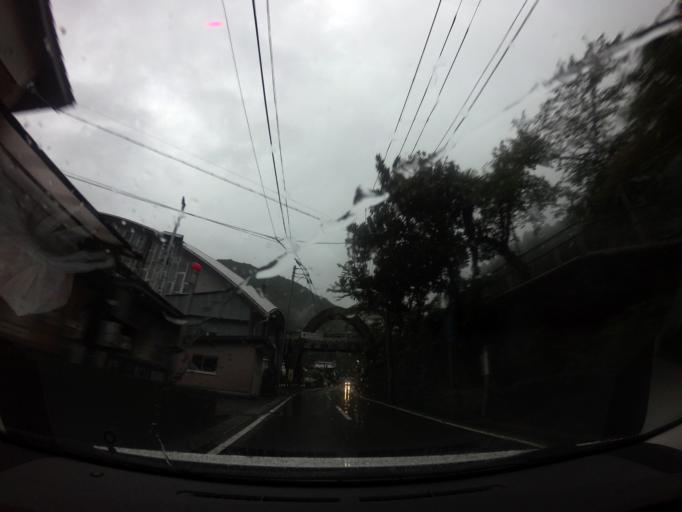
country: JP
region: Wakayama
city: Shingu
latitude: 33.9492
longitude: 135.8025
